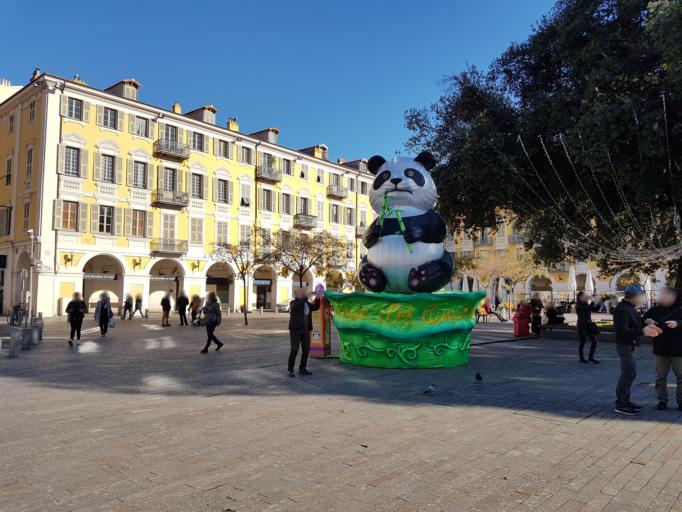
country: FR
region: Provence-Alpes-Cote d'Azur
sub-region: Departement des Alpes-Maritimes
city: Nice
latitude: 43.7010
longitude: 7.2801
